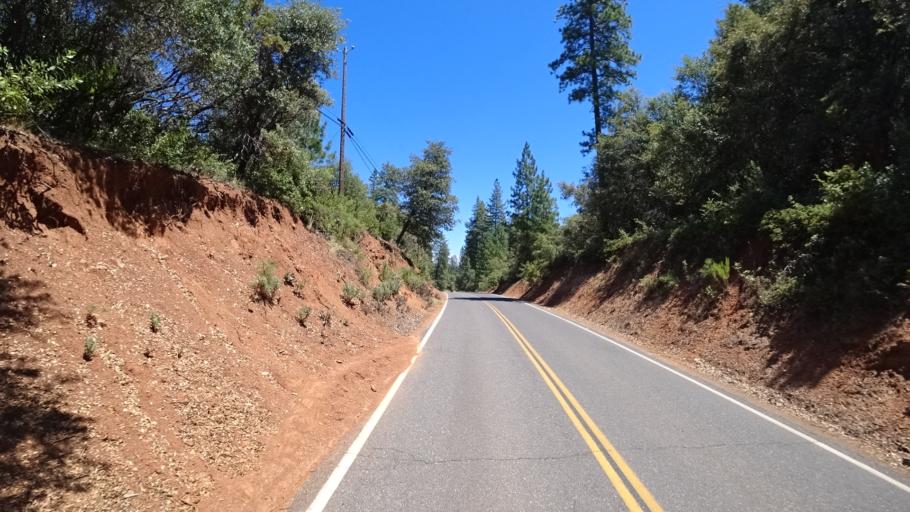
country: US
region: California
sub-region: Calaveras County
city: Murphys
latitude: 38.1396
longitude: -120.4884
